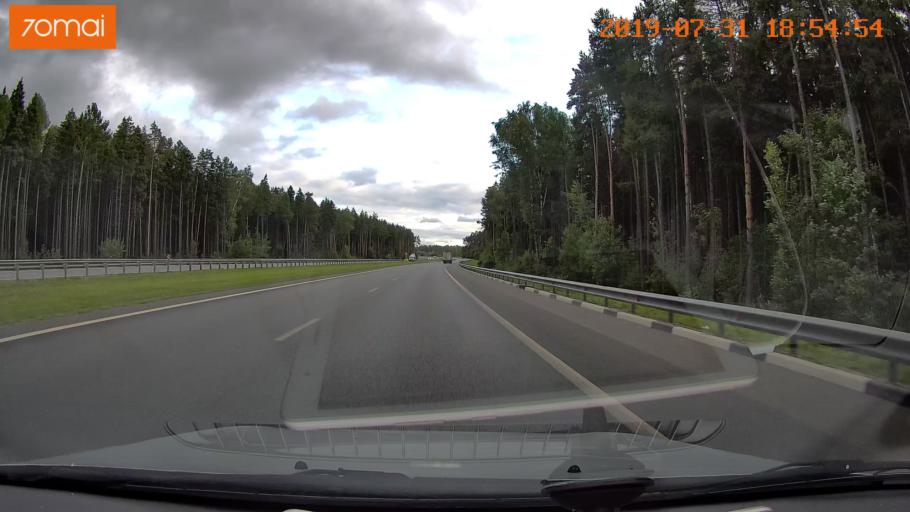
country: RU
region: Moskovskaya
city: Raduzhnyy
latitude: 55.1828
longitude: 38.6692
